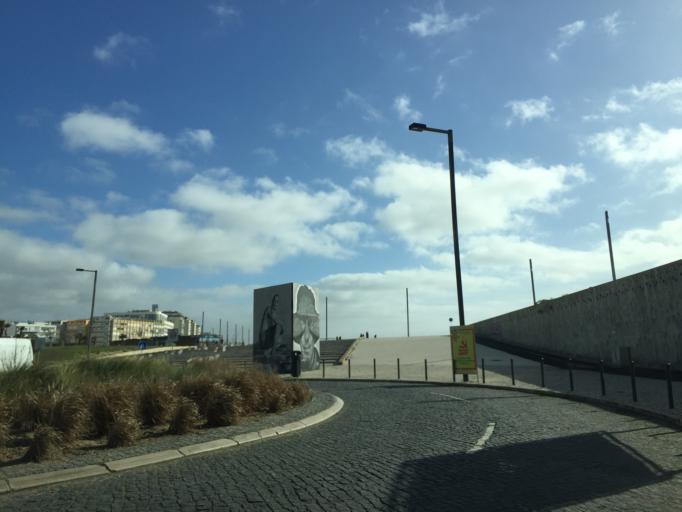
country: PT
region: Setubal
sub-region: Almada
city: Costa de Caparica
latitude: 38.6441
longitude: -9.2406
